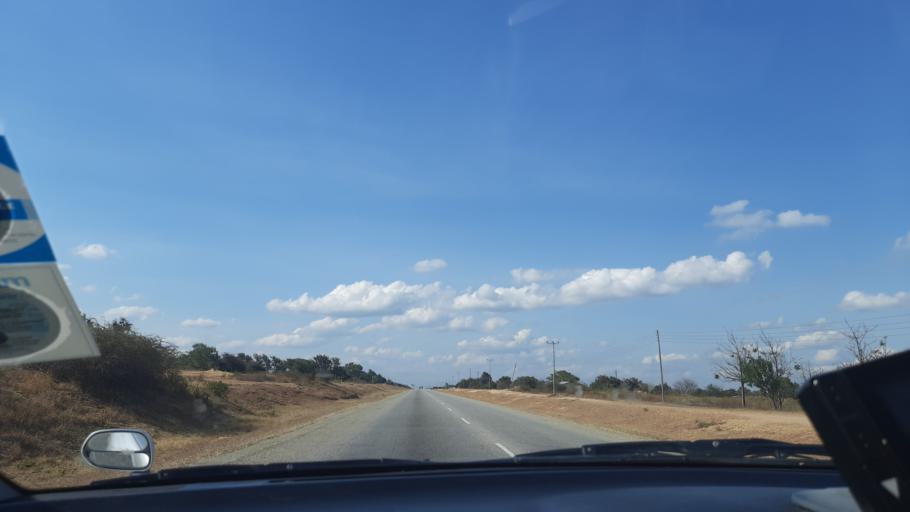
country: TZ
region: Singida
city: Itigi
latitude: -5.5487
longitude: 34.6654
